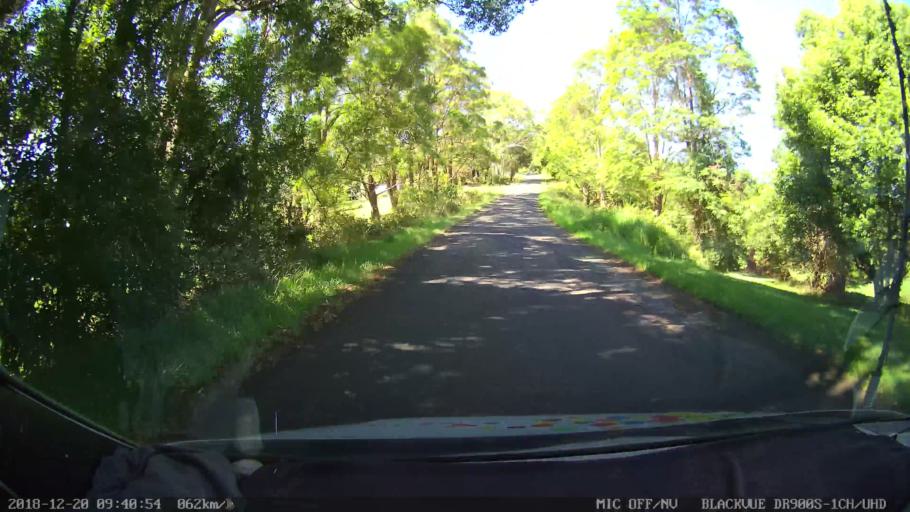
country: AU
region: New South Wales
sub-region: Lismore Municipality
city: Lismore
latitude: -28.7048
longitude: 153.3028
